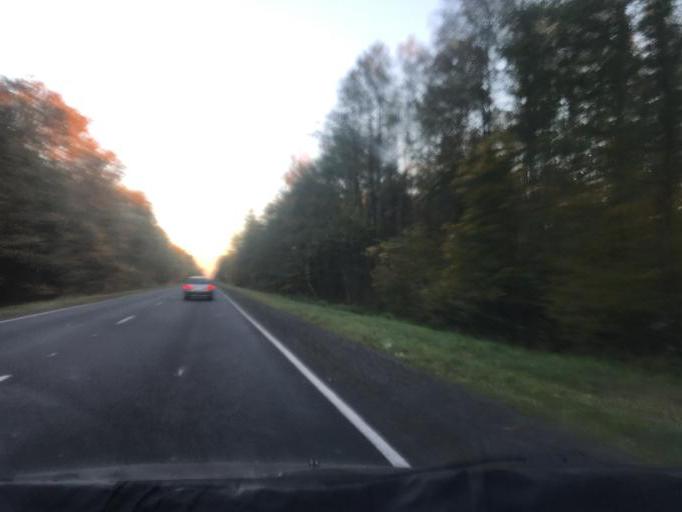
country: BY
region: Gomel
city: Mazyr
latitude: 52.1845
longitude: 29.1498
